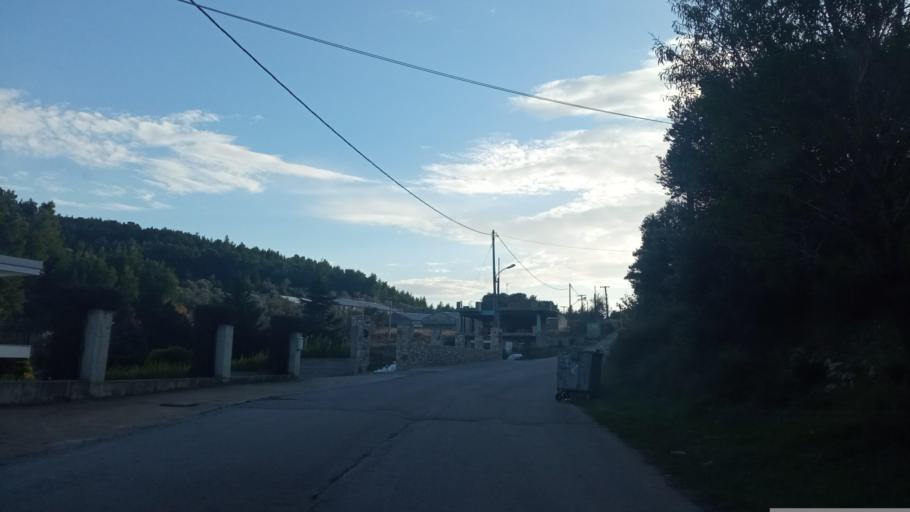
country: GR
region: Central Greece
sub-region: Nomos Evvoias
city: Psachna
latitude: 38.6139
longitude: 23.7316
